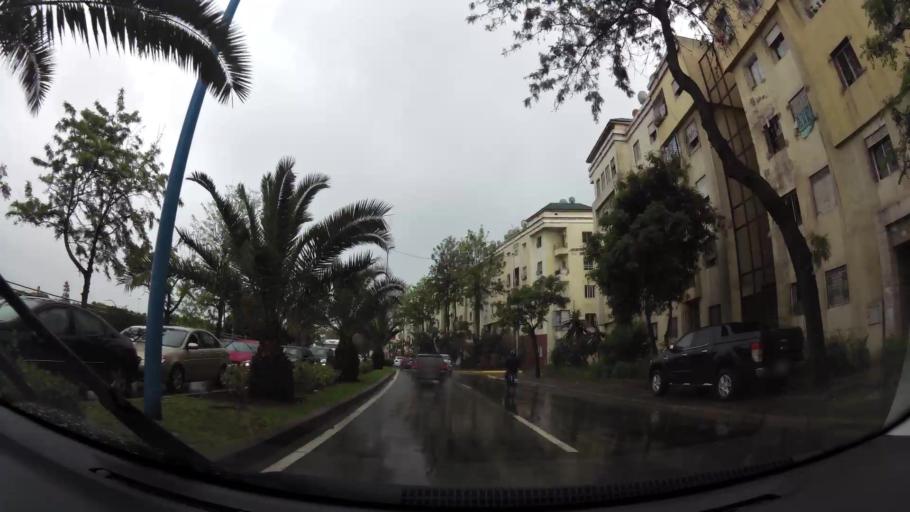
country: MA
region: Grand Casablanca
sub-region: Casablanca
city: Casablanca
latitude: 33.5596
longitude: -7.6692
